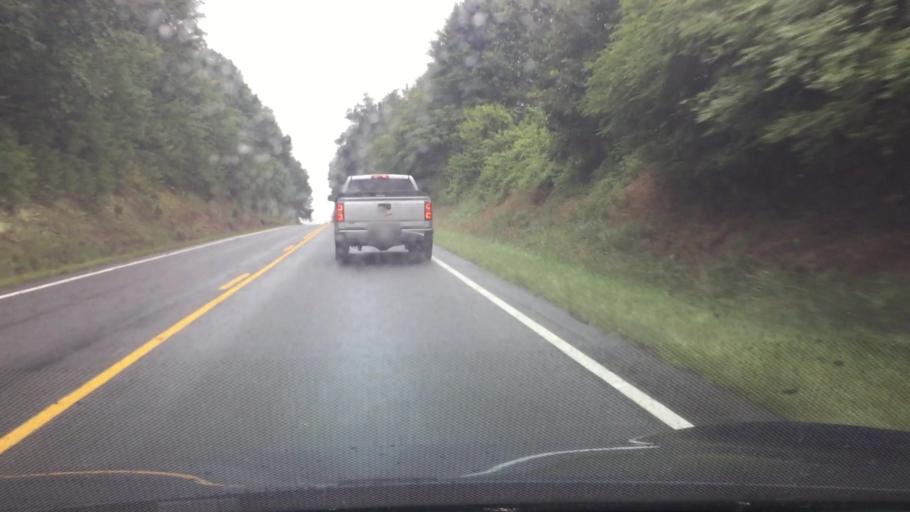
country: US
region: Virginia
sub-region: Bedford County
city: Forest
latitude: 37.3760
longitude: -79.3761
